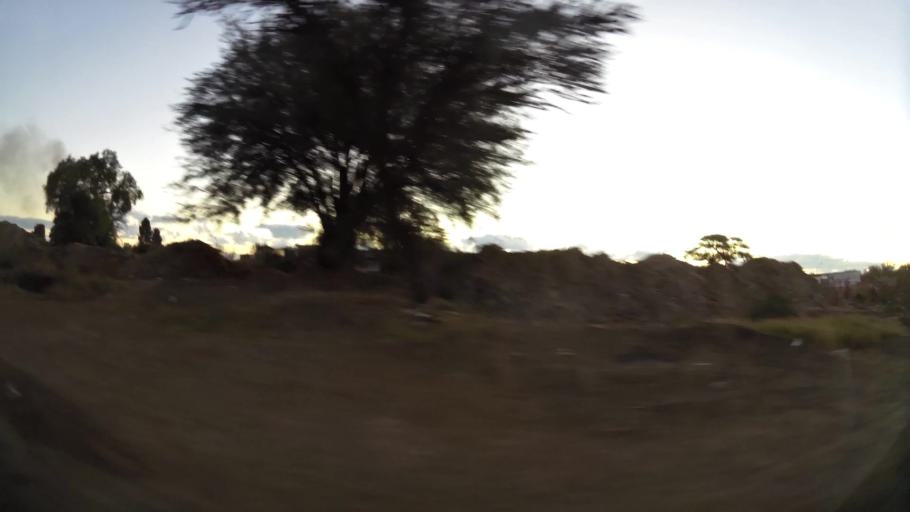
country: ZA
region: Northern Cape
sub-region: Frances Baard District Municipality
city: Kimberley
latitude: -28.7215
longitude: 24.7625
